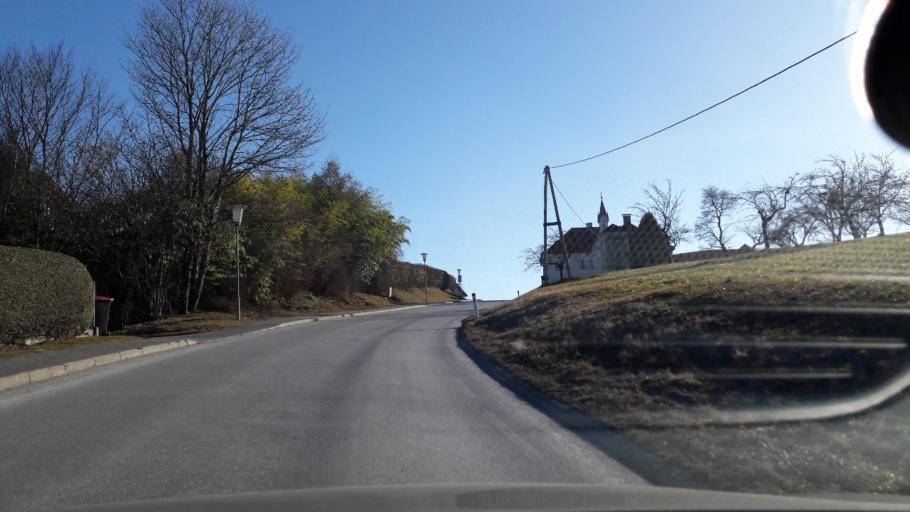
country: AT
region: Styria
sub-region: Politischer Bezirk Graz-Umgebung
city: Eisbach
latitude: 47.1332
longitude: 15.2877
